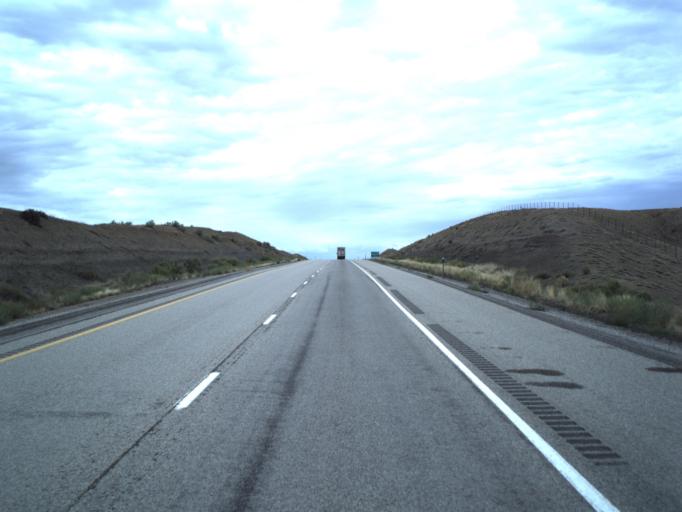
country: US
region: Colorado
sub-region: Mesa County
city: Loma
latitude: 39.0250
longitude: -109.2945
